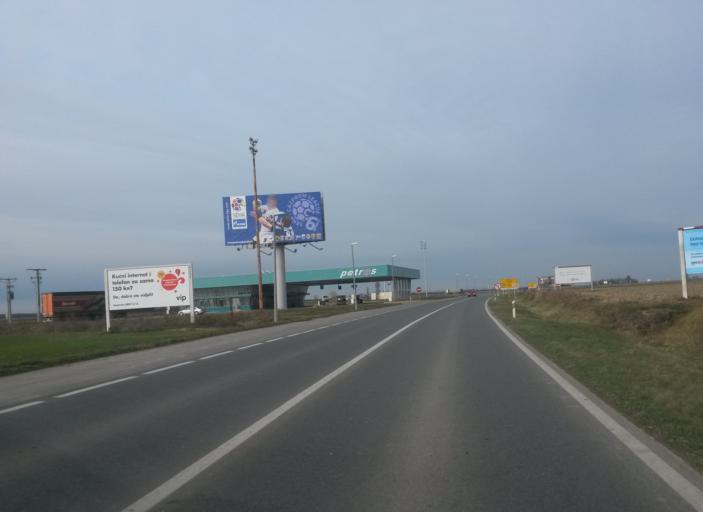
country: HR
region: Osjecko-Baranjska
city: Cepin
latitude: 45.5118
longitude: 18.5387
